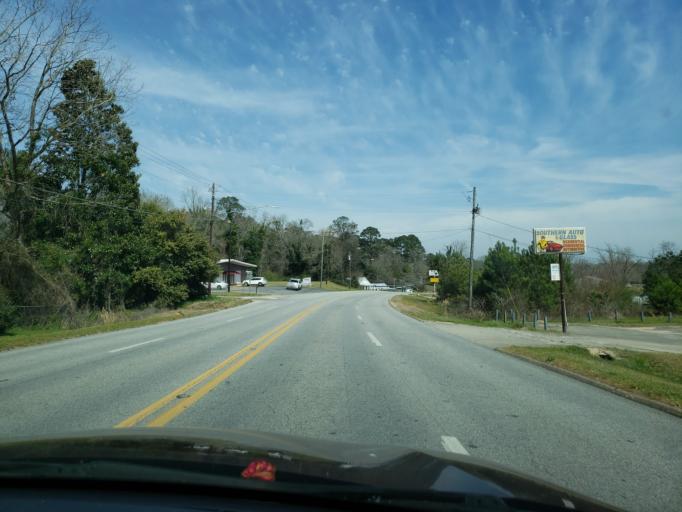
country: US
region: Alabama
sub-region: Elmore County
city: Tallassee
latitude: 32.5507
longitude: -85.8684
